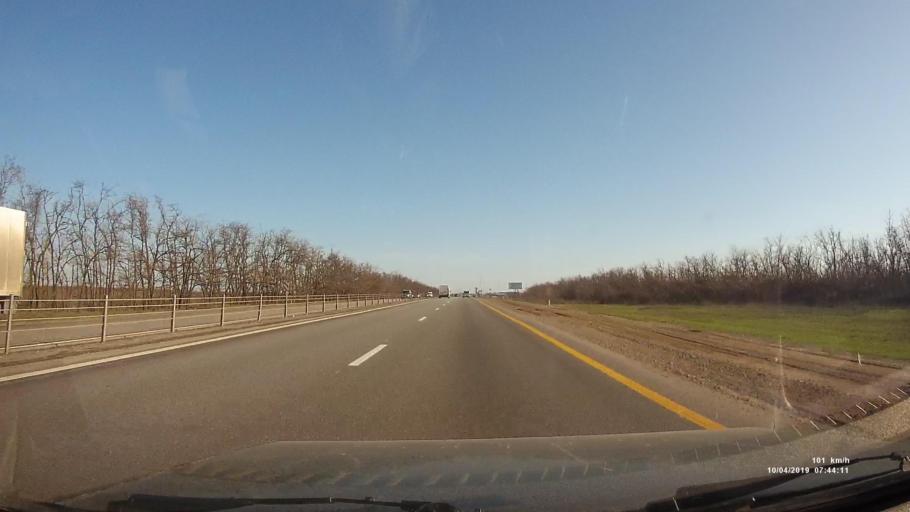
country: RU
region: Rostov
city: Likhoy
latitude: 48.1742
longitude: 40.2642
